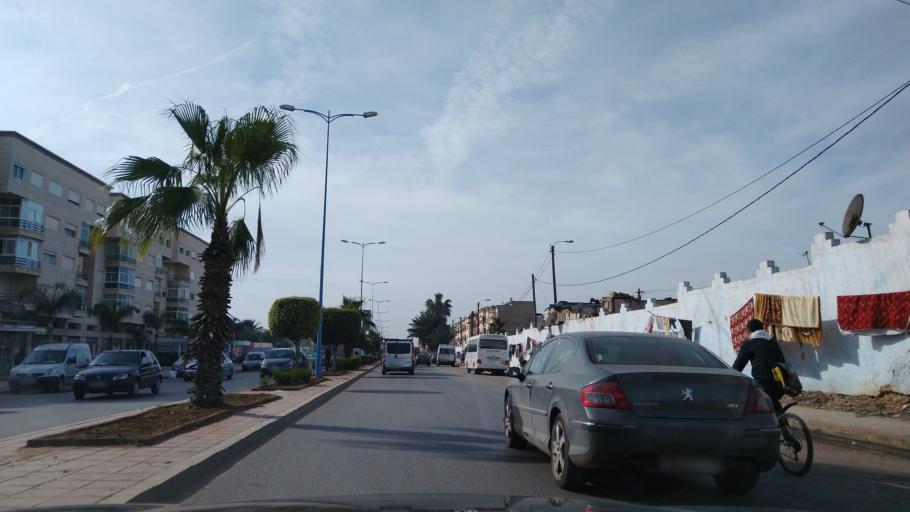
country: MA
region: Grand Casablanca
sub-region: Mohammedia
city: Mohammedia
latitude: 33.6905
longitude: -7.3737
